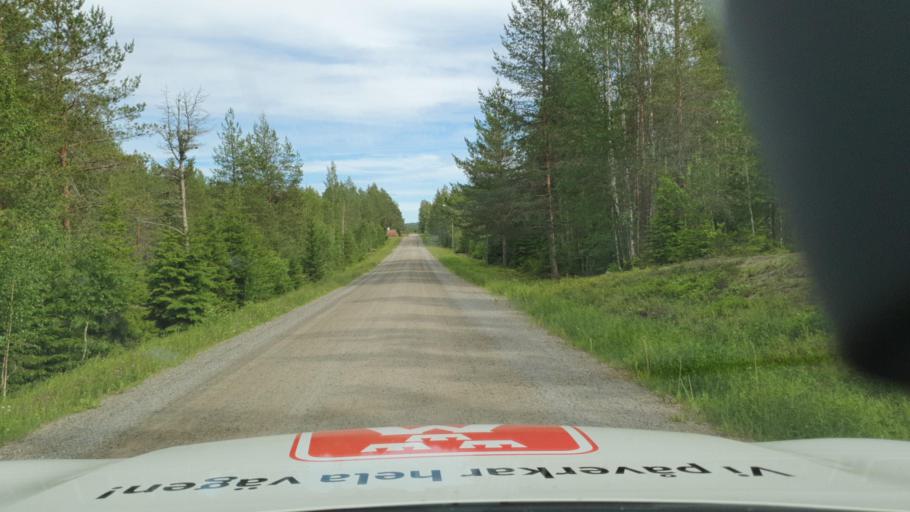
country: SE
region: Vaesterbotten
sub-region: Skelleftea Kommun
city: Burea
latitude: 64.3734
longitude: 21.0693
